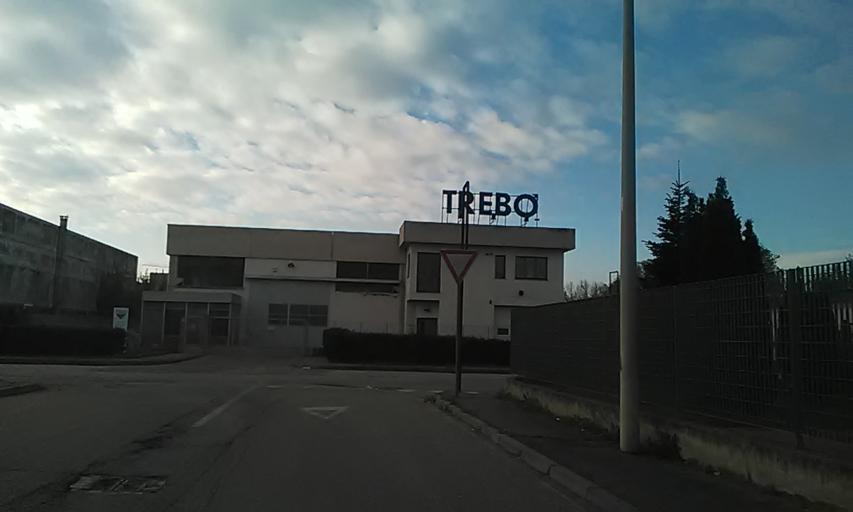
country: IT
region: Piedmont
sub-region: Provincia di Vercelli
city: Vercelli
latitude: 45.3201
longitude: 8.3966
